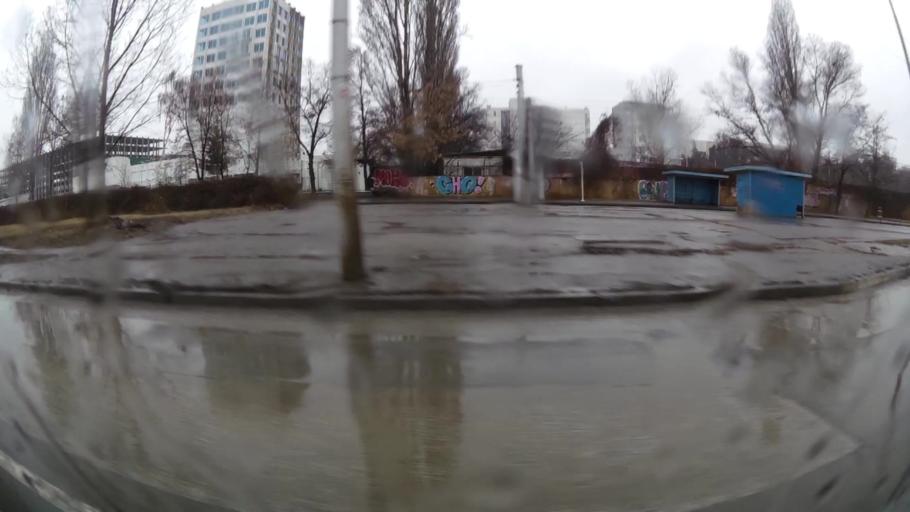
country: BG
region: Sofia-Capital
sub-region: Stolichna Obshtina
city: Sofia
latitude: 42.6737
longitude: 23.3830
